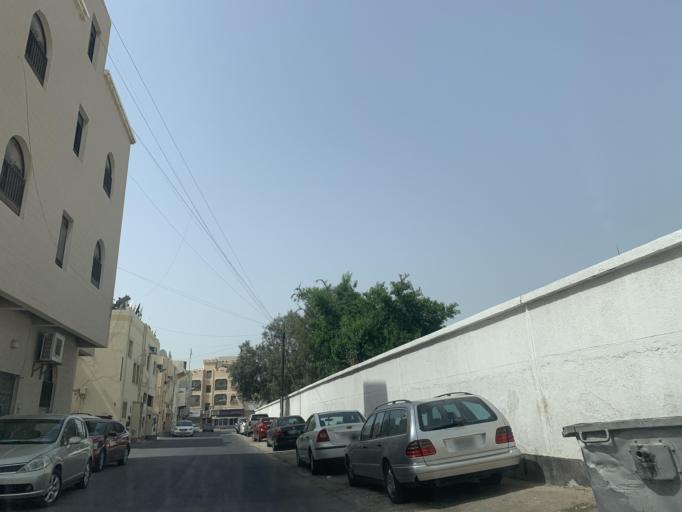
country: BH
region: Northern
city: Madinat `Isa
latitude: 26.1805
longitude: 50.5507
